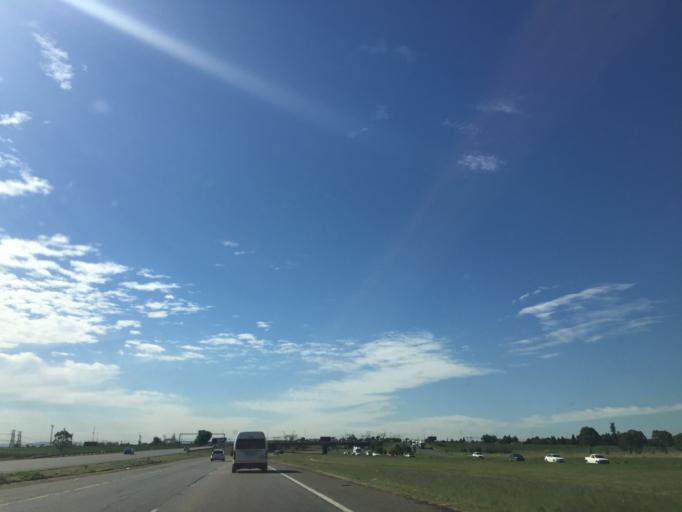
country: ZA
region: Gauteng
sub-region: Ekurhuleni Metropolitan Municipality
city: Germiston
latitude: -26.3018
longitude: 28.1103
